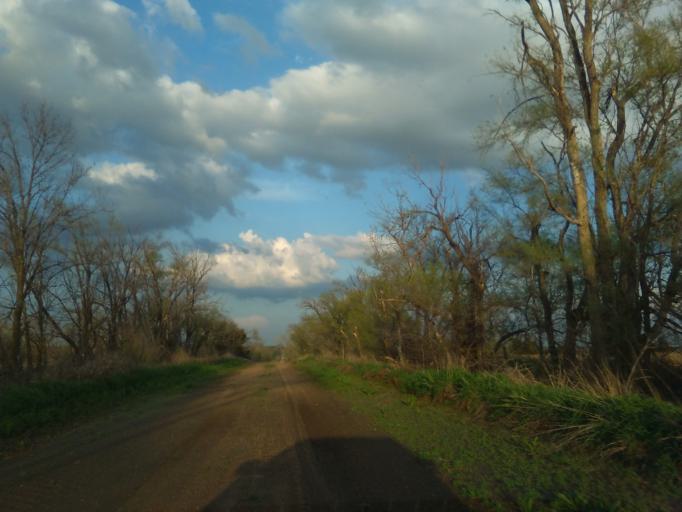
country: US
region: Nebraska
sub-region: Webster County
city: Red Cloud
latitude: 40.2054
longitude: -98.3776
